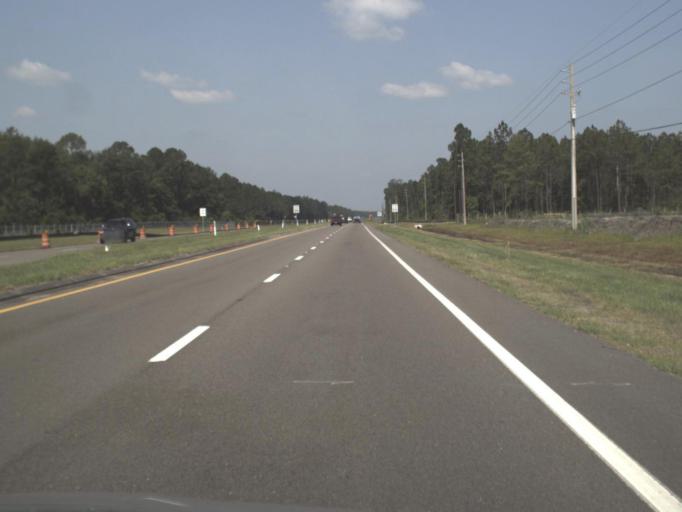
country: US
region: Florida
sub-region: Clay County
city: Bellair-Meadowbrook Terrace
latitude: 30.2470
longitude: -81.8489
